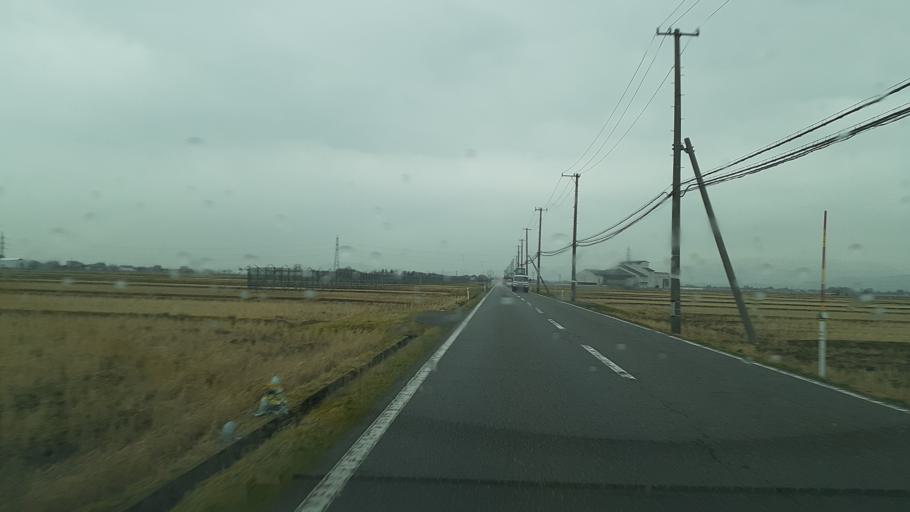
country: JP
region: Niigata
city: Suibara
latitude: 37.8852
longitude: 139.1786
